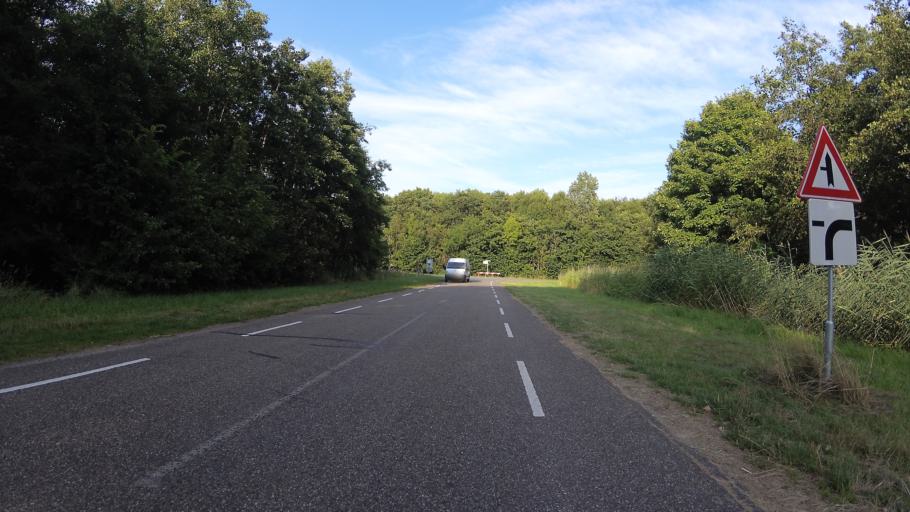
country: NL
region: Zeeland
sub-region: Gemeente Veere
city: Veere
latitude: 51.5740
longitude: 3.6607
